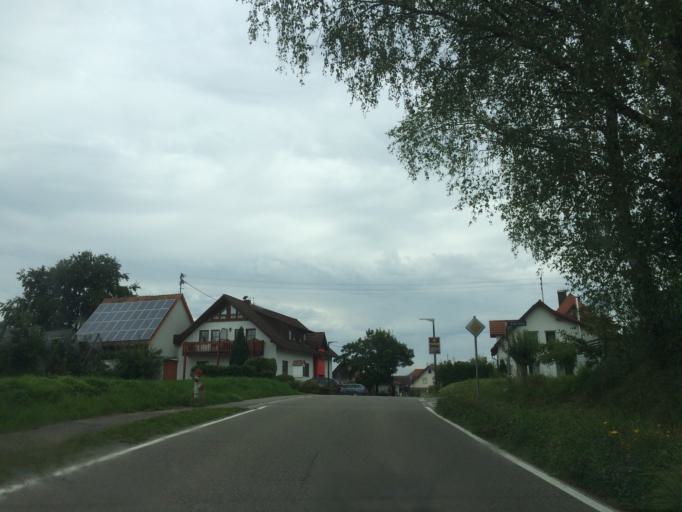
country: DE
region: Baden-Wuerttemberg
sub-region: Tuebingen Region
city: Hagnau
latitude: 47.6979
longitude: 9.3415
